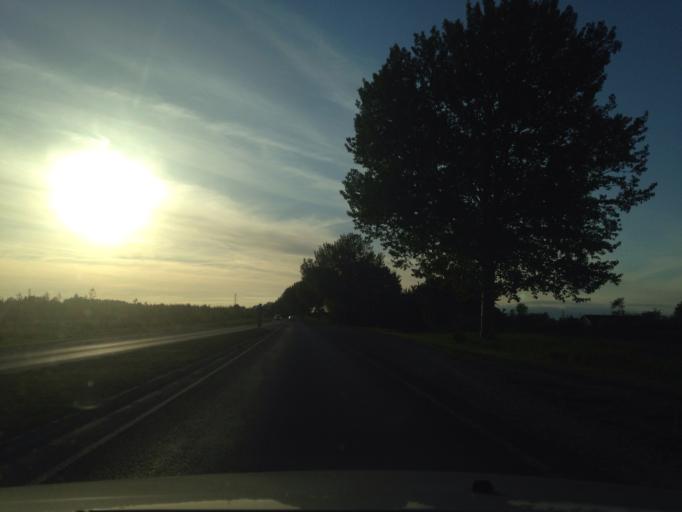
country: DK
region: Zealand
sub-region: Greve Kommune
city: Tune
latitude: 55.5996
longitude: 12.2260
